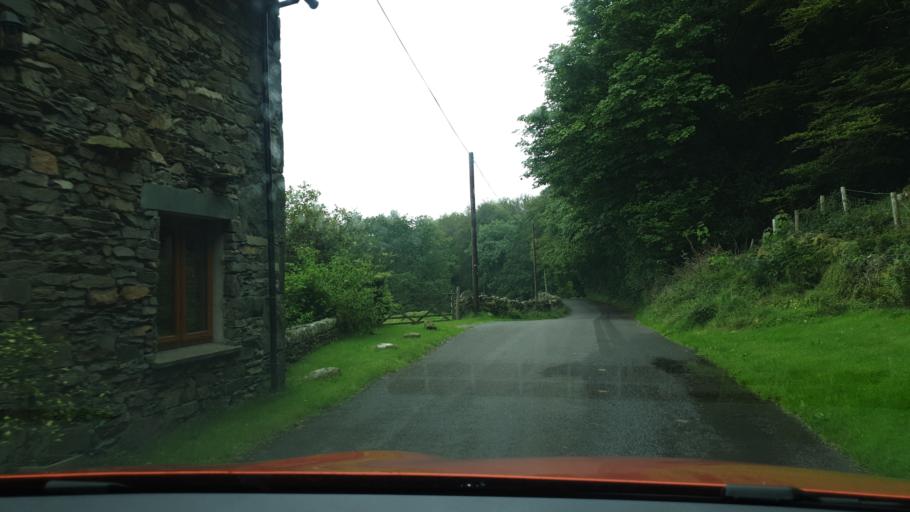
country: GB
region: England
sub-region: Cumbria
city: Grange-over-Sands
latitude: 54.2746
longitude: -2.9851
